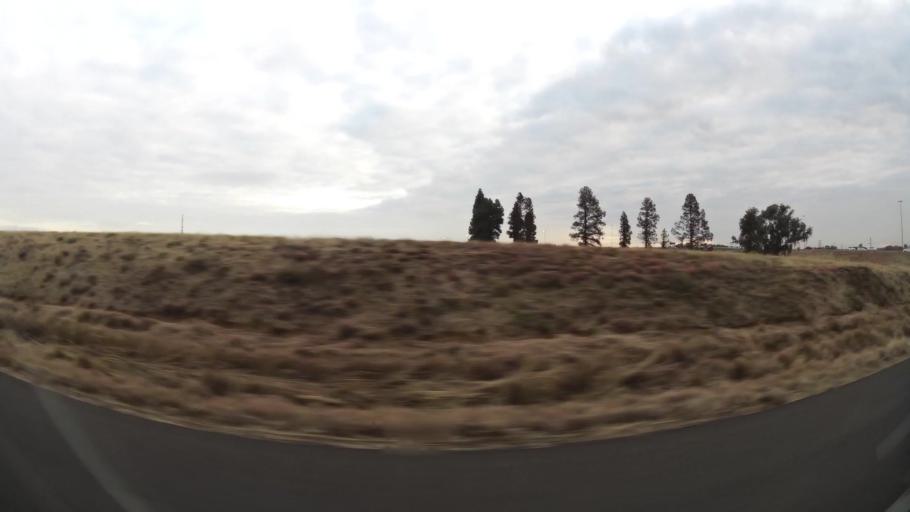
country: ZA
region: Orange Free State
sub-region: Mangaung Metropolitan Municipality
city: Bloemfontein
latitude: -29.0925
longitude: 26.1709
